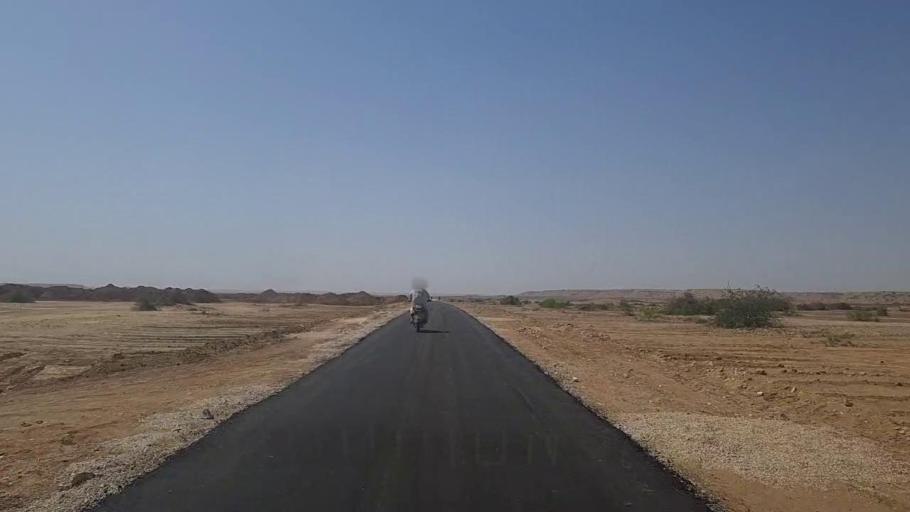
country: PK
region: Sindh
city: Kotri
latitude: 25.1463
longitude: 68.1985
